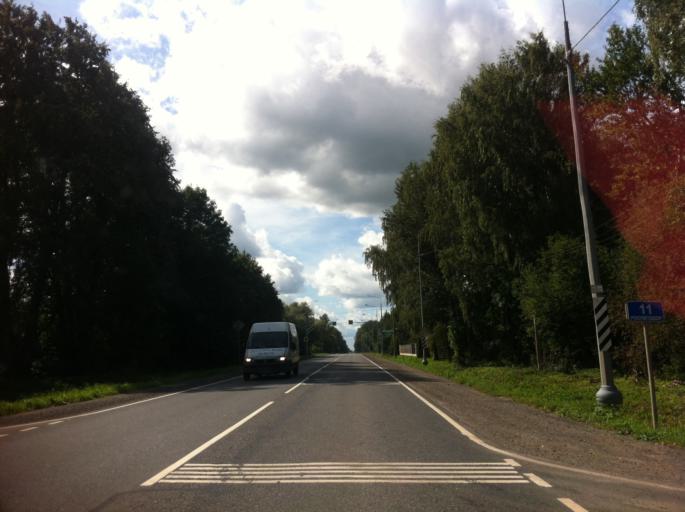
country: RU
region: Pskov
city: Pskov
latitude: 57.7801
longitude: 28.1636
